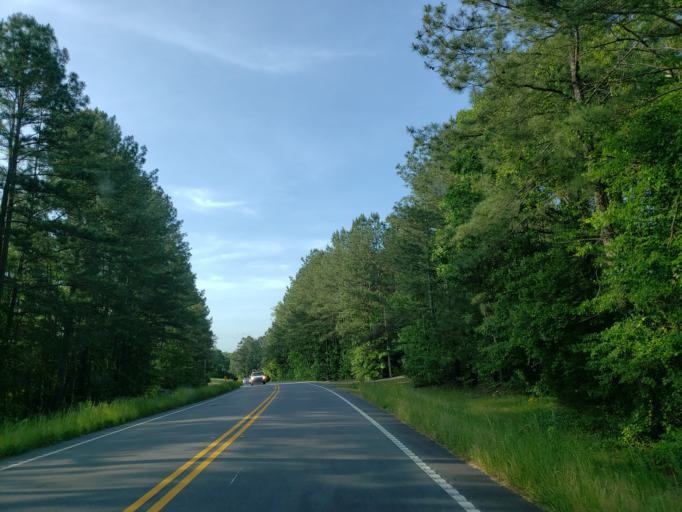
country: US
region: Georgia
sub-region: Carroll County
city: Bowdon
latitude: 33.5615
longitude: -85.2510
